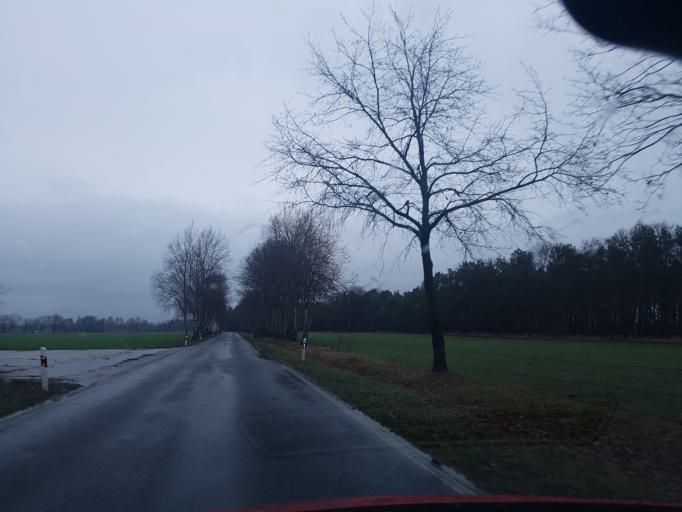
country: DE
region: Brandenburg
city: Schilda
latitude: 51.6173
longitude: 13.3189
